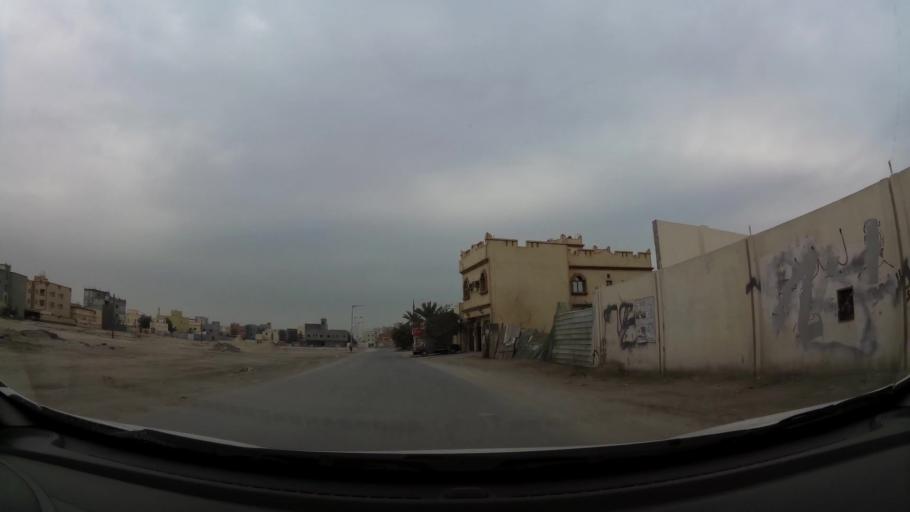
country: BH
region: Northern
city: Sitrah
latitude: 26.1406
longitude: 50.6093
